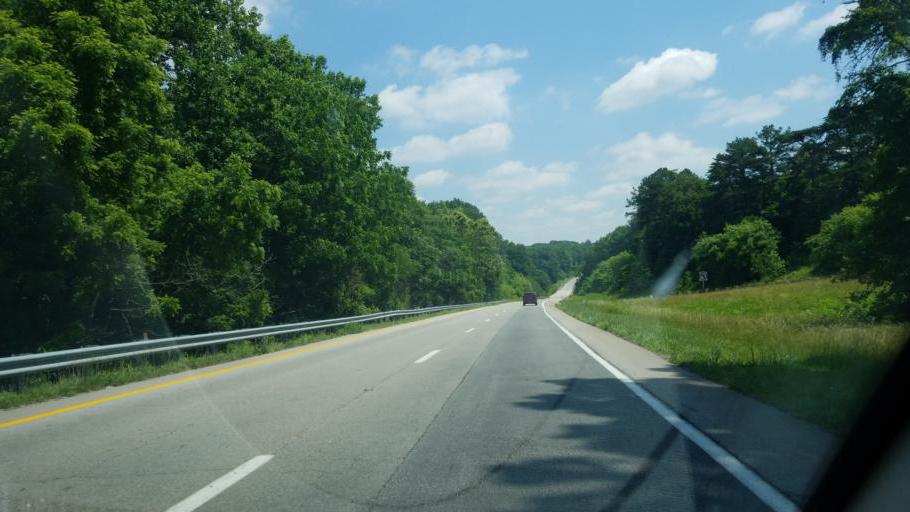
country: US
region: Virginia
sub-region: Pittsylvania County
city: Hurt
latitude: 37.1166
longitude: -79.3250
